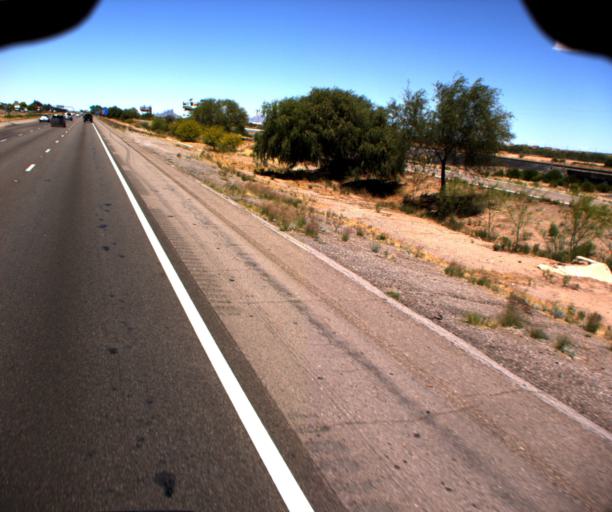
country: US
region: Arizona
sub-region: Pima County
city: Marana
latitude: 32.4496
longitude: -111.1985
